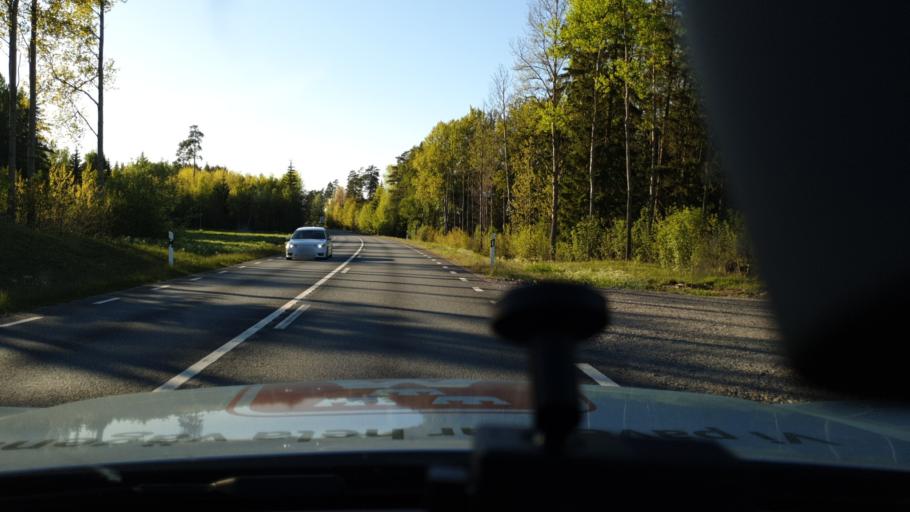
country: SE
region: Joenkoeping
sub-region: Vetlanda Kommun
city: Ekenassjon
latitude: 57.5472
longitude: 14.9921
